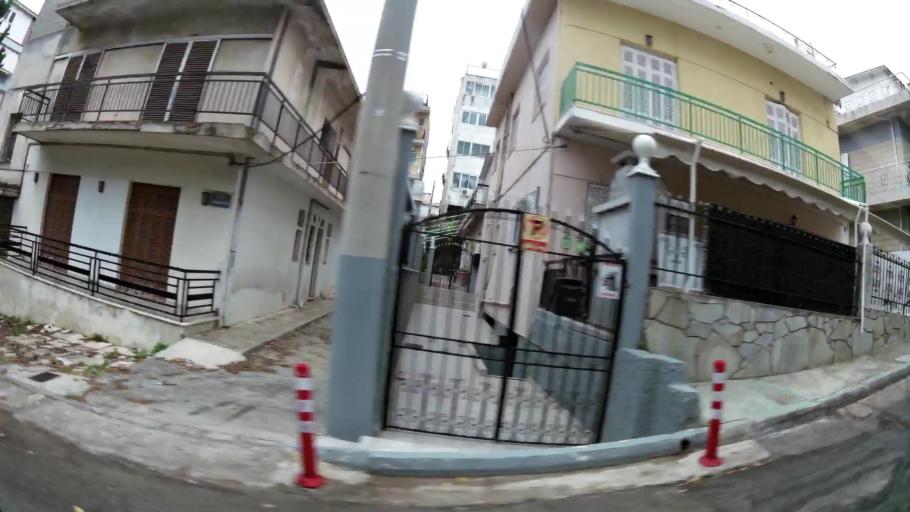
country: GR
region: Attica
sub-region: Nomarchia Athinas
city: Chaidari
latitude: 38.0111
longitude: 23.6638
